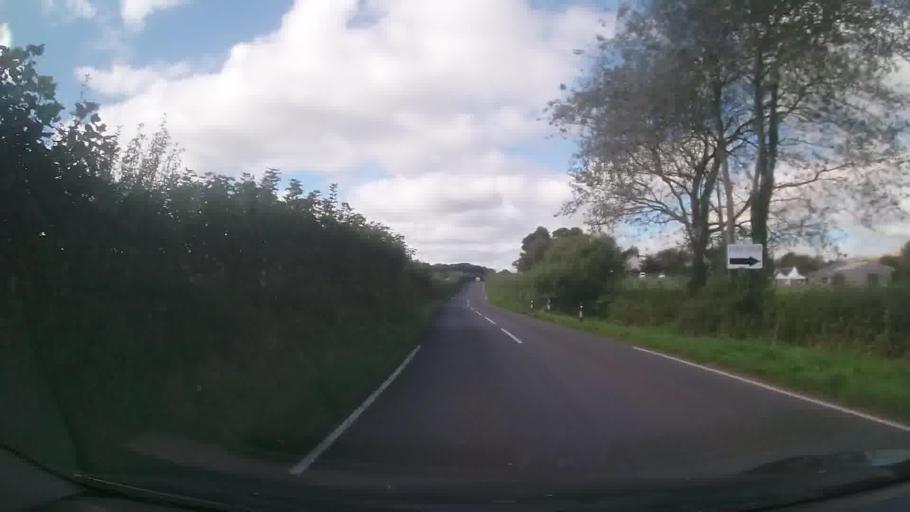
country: GB
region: Wales
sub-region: Pembrokeshire
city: Penally
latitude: 51.6568
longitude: -4.7470
